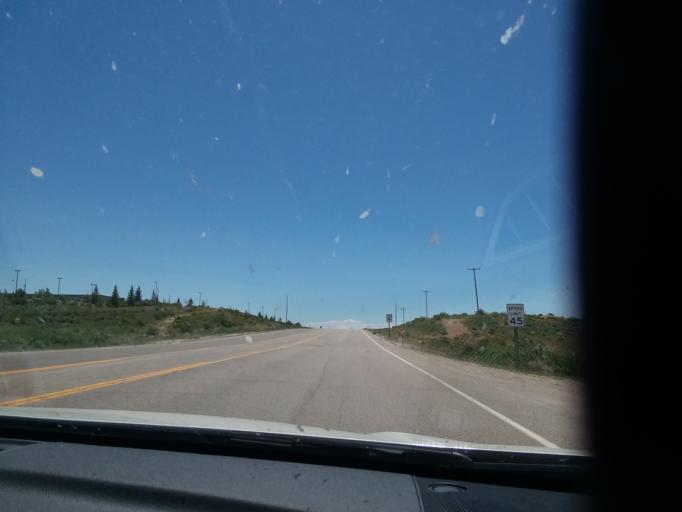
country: US
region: Wyoming
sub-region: Sweetwater County
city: North Rock Springs
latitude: 41.6303
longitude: -109.2317
